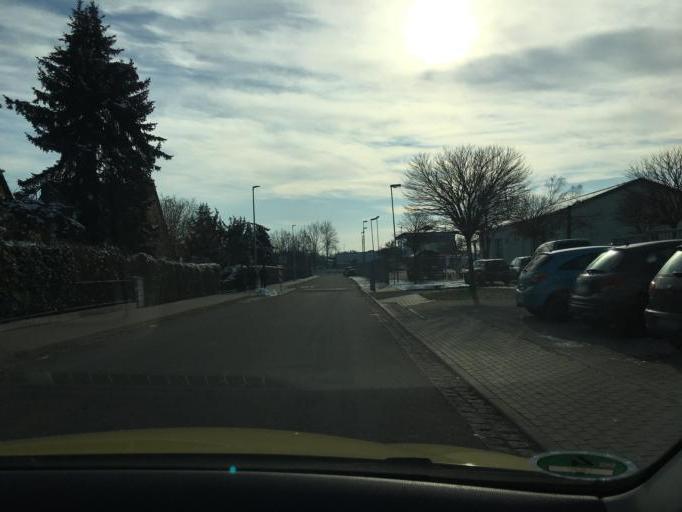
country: DE
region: Saxony
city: Bad Lausick
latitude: 51.1447
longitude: 12.6489
